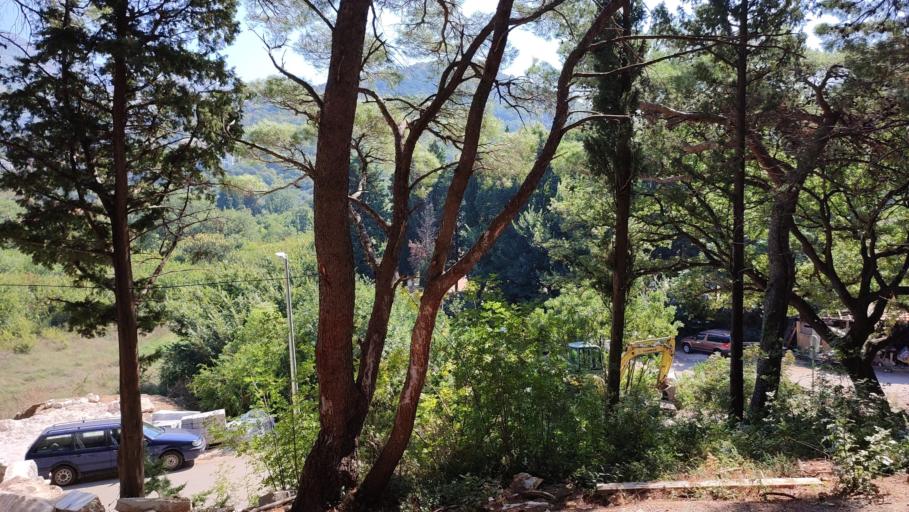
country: ME
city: Petrovac na Moru
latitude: 42.2015
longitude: 18.9501
